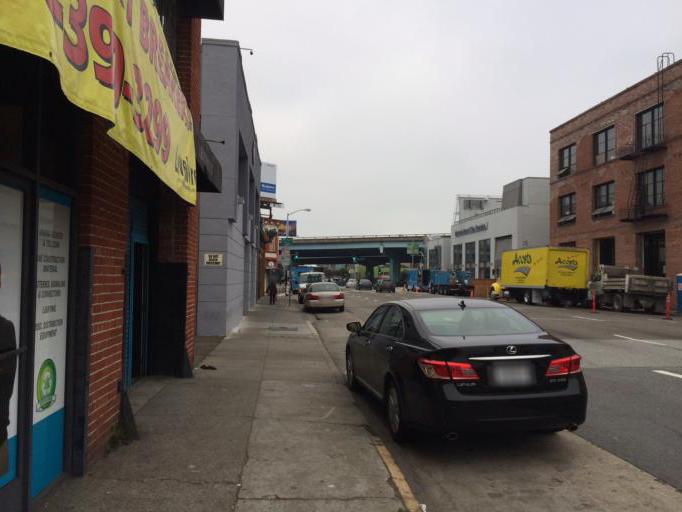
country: US
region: California
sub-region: San Francisco County
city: San Francisco
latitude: 37.7718
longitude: -122.4081
